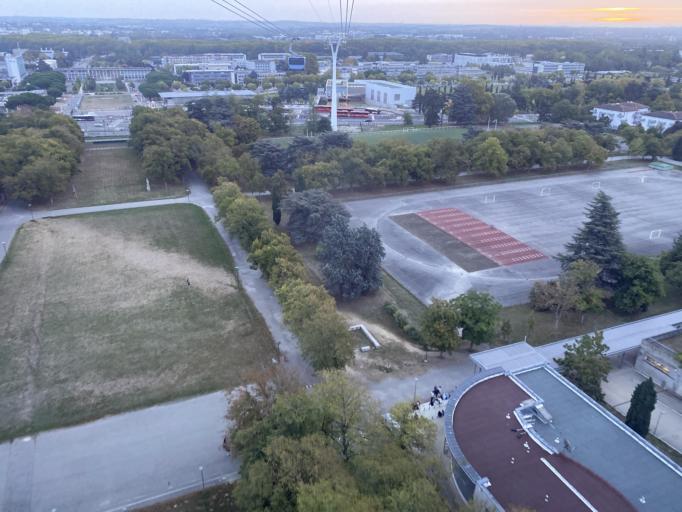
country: FR
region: Midi-Pyrenees
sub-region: Departement de la Haute-Garonne
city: Ramonville-Saint-Agne
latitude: 43.5593
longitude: 1.4594
